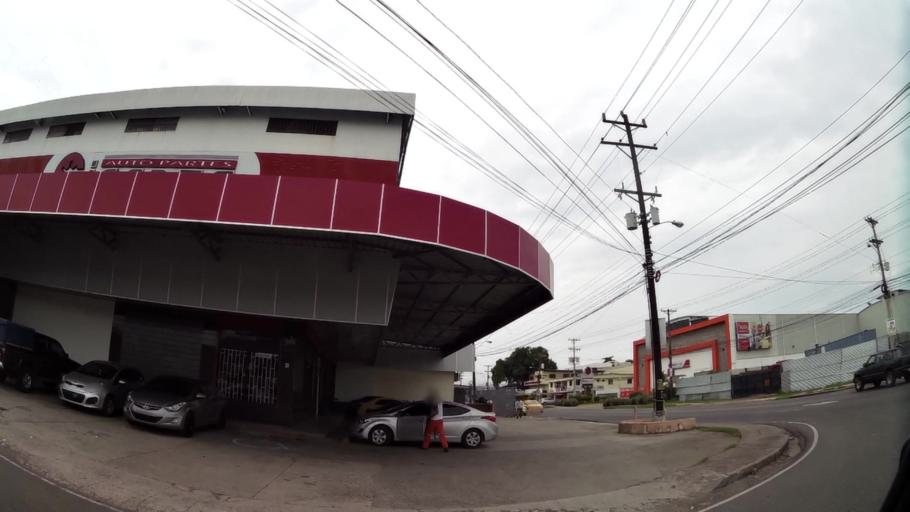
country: PA
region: Panama
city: San Miguelito
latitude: 9.0464
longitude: -79.4434
